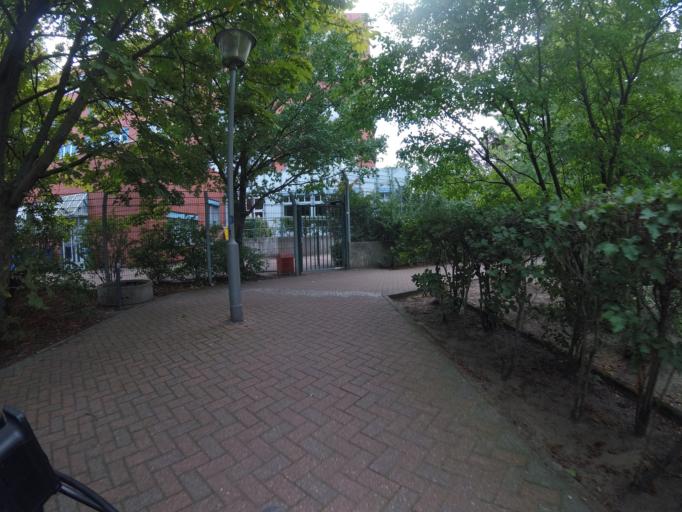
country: DE
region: Berlin
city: Haselhorst
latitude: 52.5402
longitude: 13.2419
